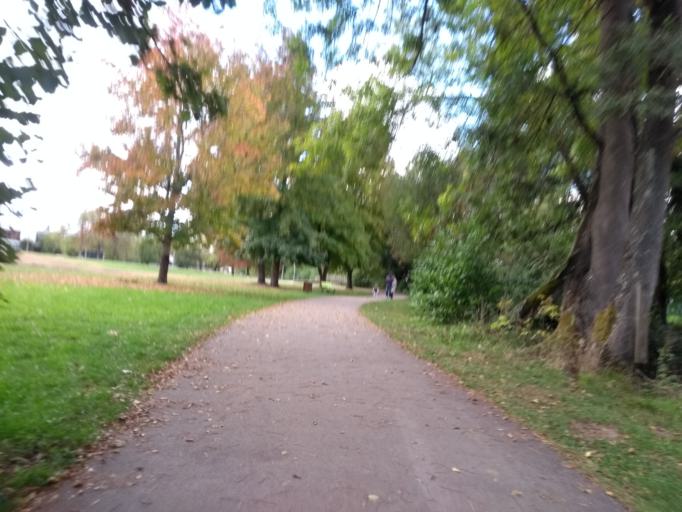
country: FR
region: Aquitaine
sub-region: Departement de la Gironde
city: Gradignan
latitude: 44.7685
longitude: -0.6082
